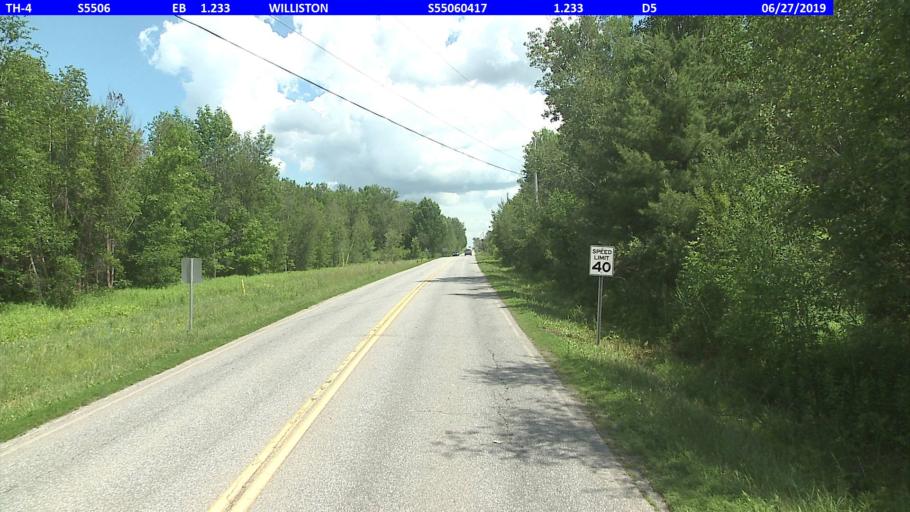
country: US
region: Vermont
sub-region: Chittenden County
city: Williston
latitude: 44.4609
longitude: -73.0902
